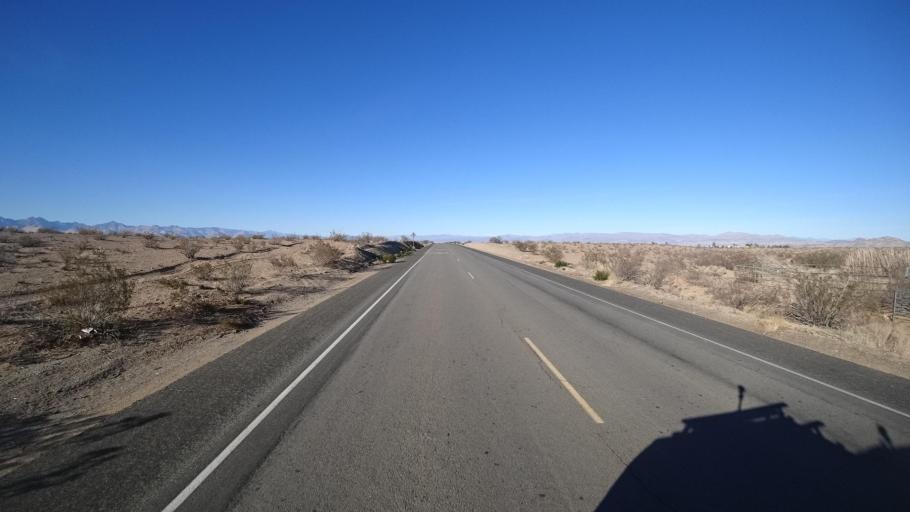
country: US
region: California
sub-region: Kern County
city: China Lake Acres
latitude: 35.6095
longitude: -117.7230
